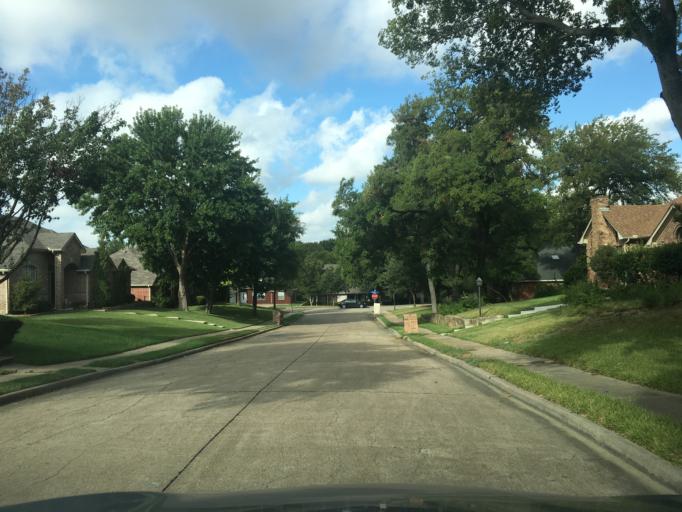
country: US
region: Texas
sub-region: Dallas County
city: Sachse
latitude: 32.9658
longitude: -96.5920
